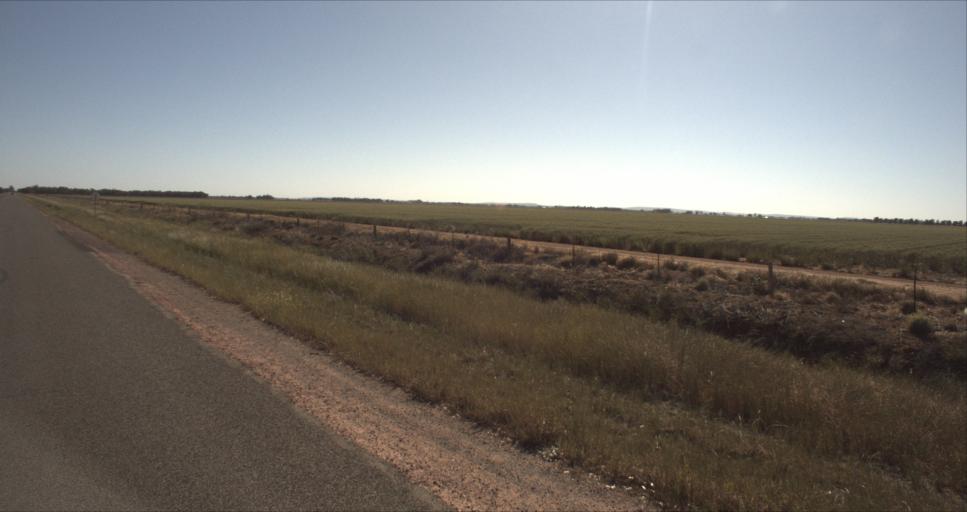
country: AU
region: New South Wales
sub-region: Leeton
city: Leeton
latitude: -34.5770
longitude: 146.2623
